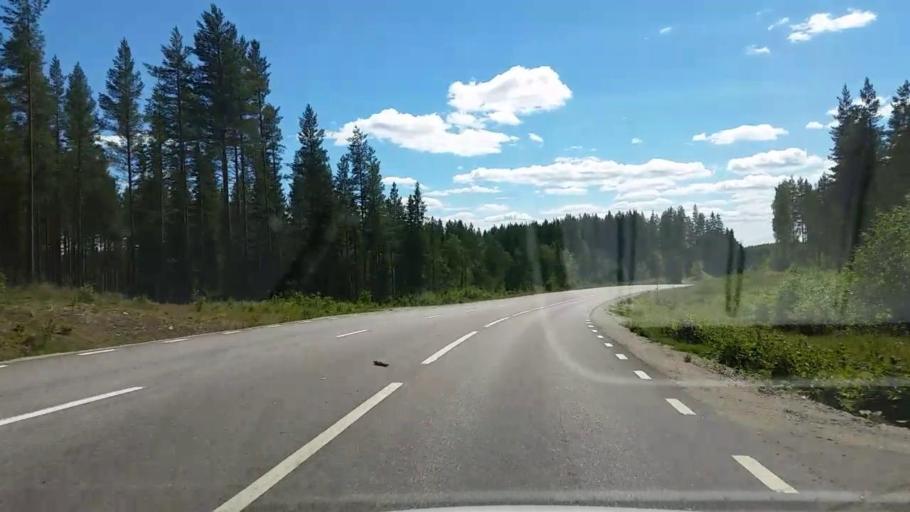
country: SE
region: Gaevleborg
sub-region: Bollnas Kommun
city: Vittsjo
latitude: 61.0507
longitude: 15.8007
